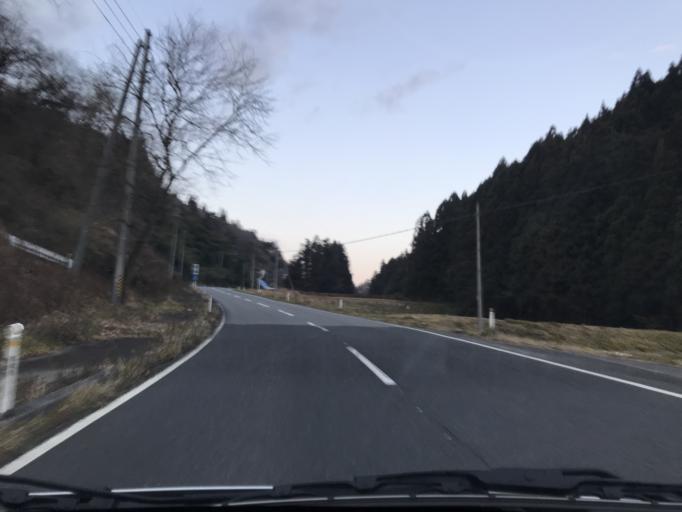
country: JP
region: Iwate
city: Ichinoseki
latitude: 38.8206
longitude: 141.1174
